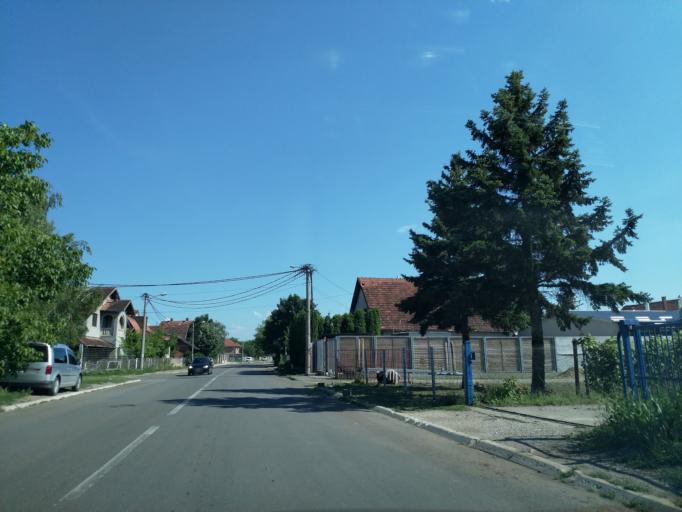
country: RS
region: Central Serbia
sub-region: Pomoravski Okrug
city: Paracin
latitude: 43.8504
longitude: 21.4110
